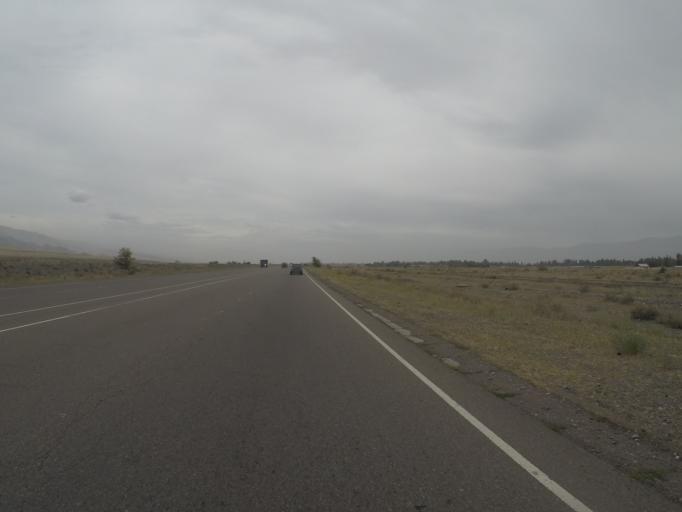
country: KG
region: Chuy
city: Bystrovka
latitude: 42.8301
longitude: 75.5164
